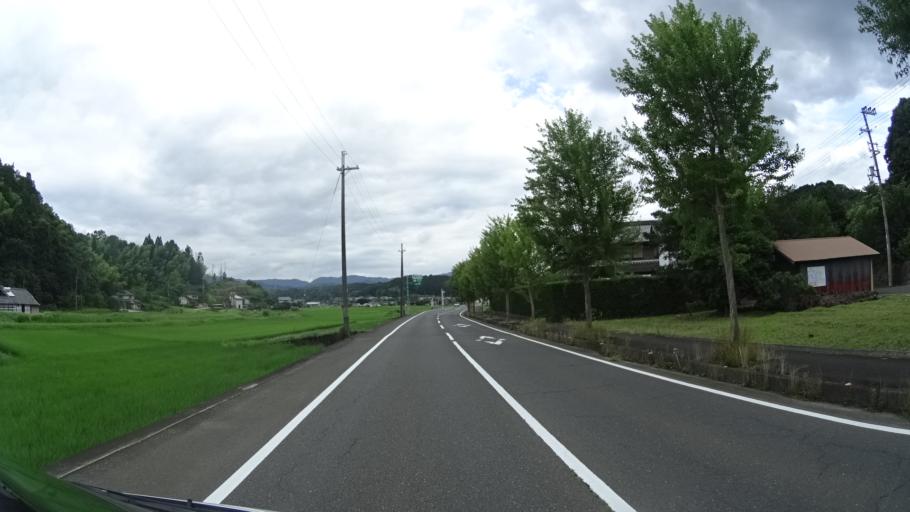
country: JP
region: Kyoto
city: Ayabe
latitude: 35.3245
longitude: 135.2617
